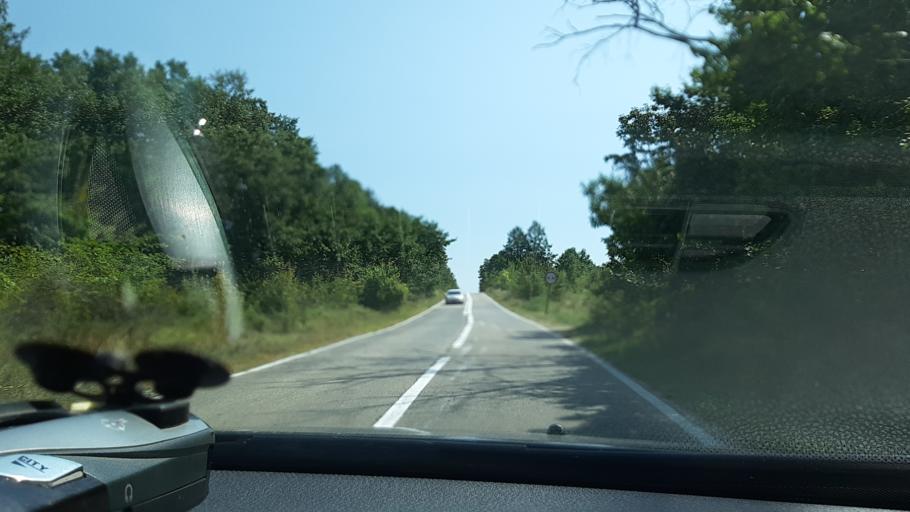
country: RO
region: Gorj
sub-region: Comuna Licuriciu
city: Licuriciu
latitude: 44.9445
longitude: 23.5756
